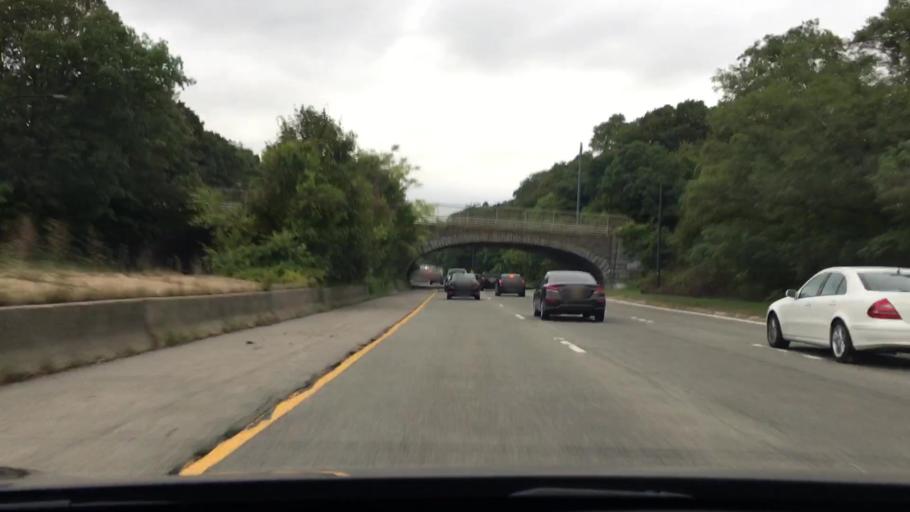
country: US
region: New York
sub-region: Nassau County
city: Albertson
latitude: 40.7809
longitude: -73.6383
